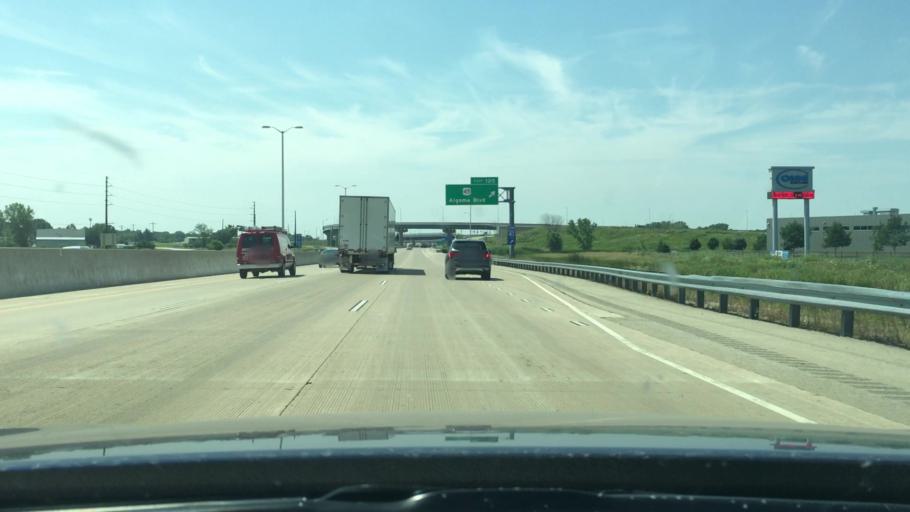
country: US
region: Wisconsin
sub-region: Winnebago County
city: Oshkosh
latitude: 44.0656
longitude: -88.5706
